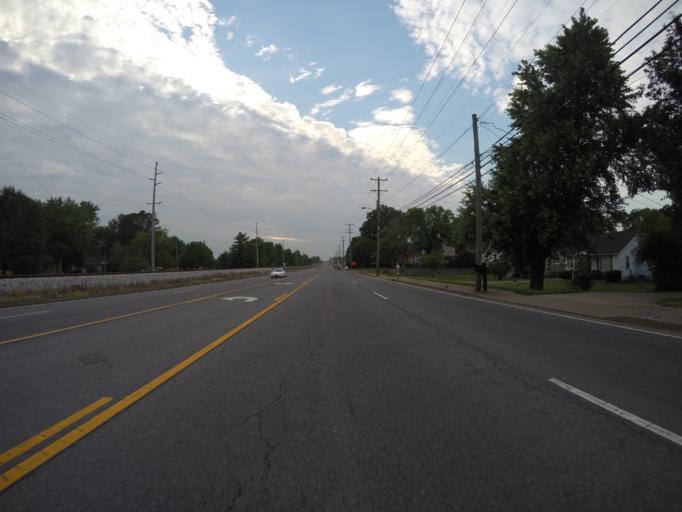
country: US
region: Tennessee
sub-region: Davidson County
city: Lakewood
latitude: 36.2394
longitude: -86.6307
